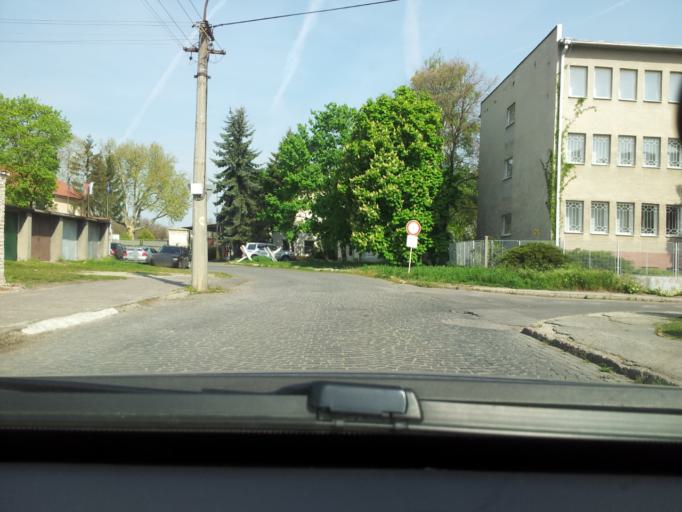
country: SK
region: Nitriansky
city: Levice
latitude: 48.2166
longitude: 18.5944
